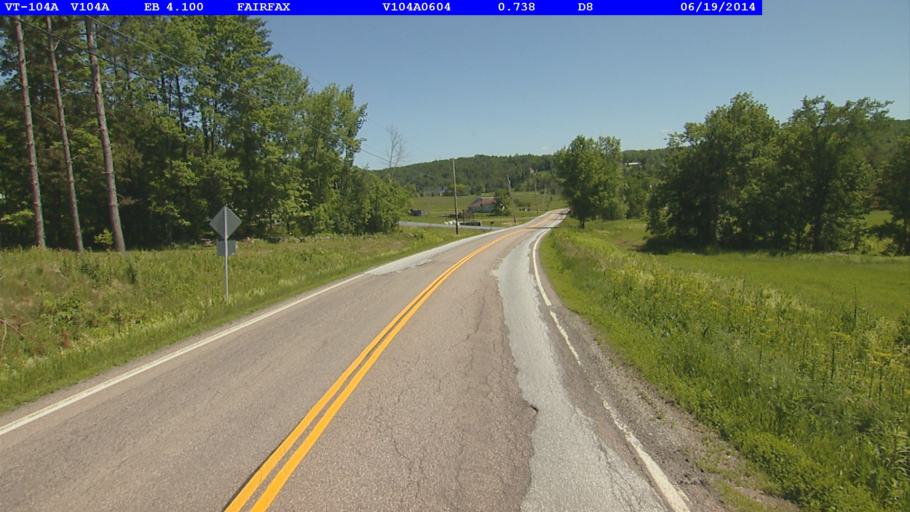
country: US
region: Vermont
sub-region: Chittenden County
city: Milton
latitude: 44.6820
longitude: -73.0373
